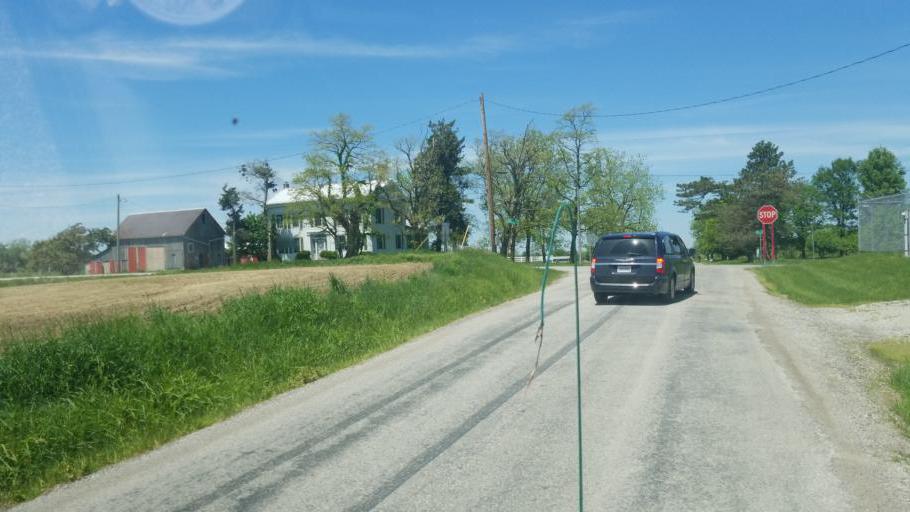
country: US
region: Ohio
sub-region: Huron County
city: New London
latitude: 41.0286
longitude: -82.4348
